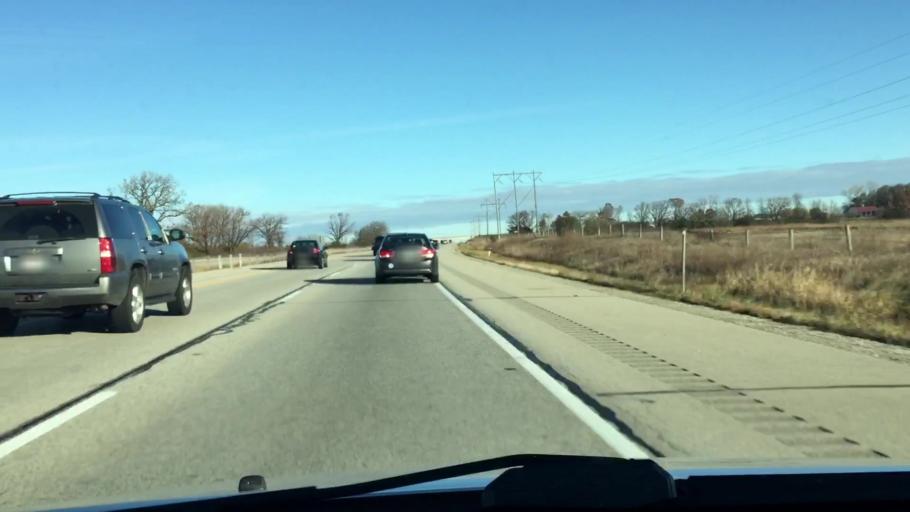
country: US
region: Wisconsin
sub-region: Fond du Lac County
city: Rosendale
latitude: 43.8642
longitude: -88.5838
